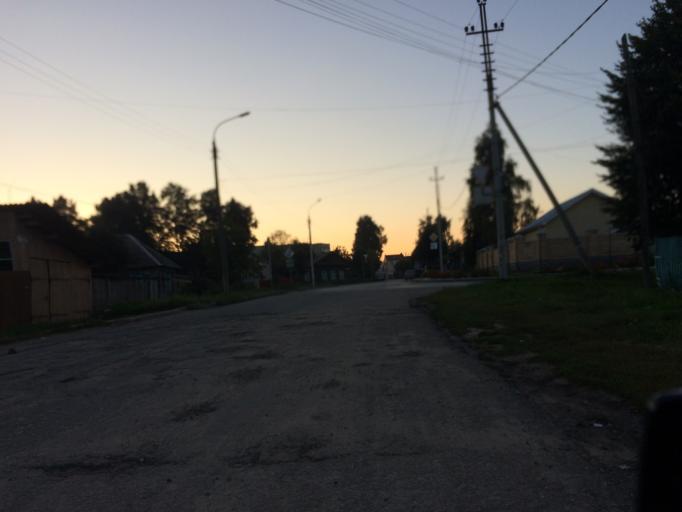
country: RU
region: Mariy-El
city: Yoshkar-Ola
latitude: 56.6436
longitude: 47.9076
